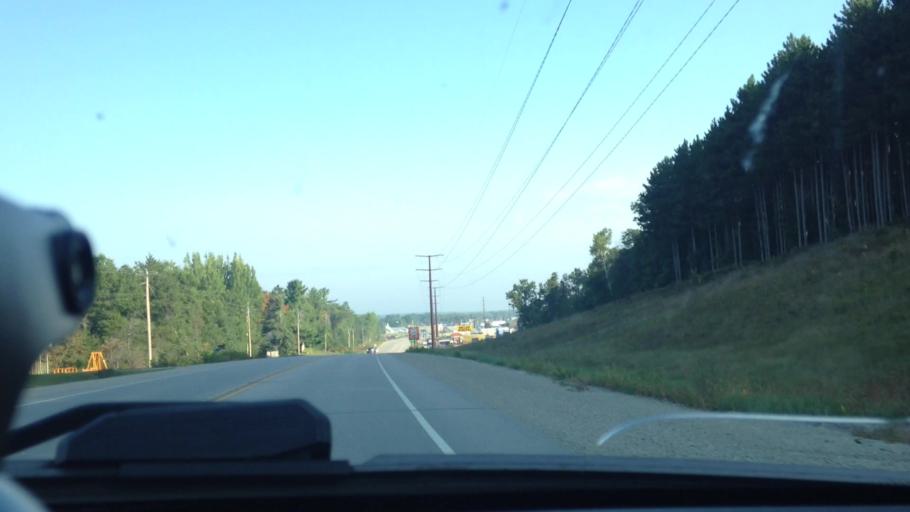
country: US
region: Wisconsin
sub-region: Marinette County
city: Peshtigo
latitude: 45.2144
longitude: -87.9959
